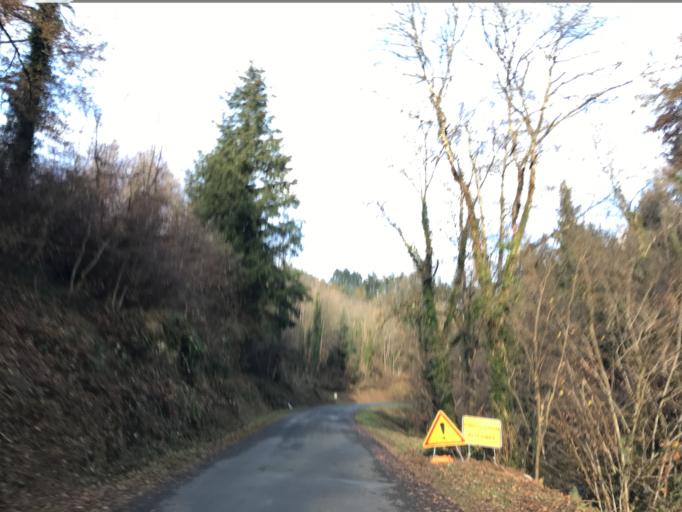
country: FR
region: Auvergne
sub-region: Departement du Puy-de-Dome
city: Courpiere
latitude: 45.7575
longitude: 3.6216
